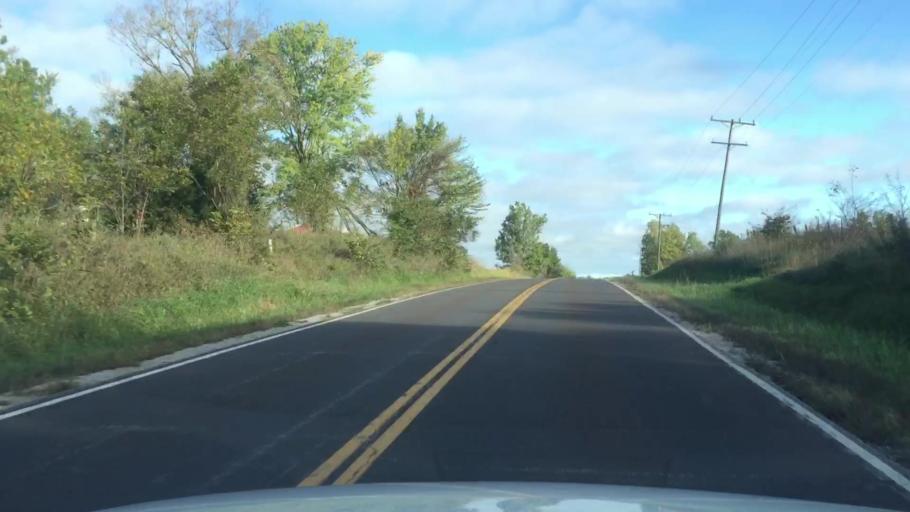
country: US
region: Missouri
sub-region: Howard County
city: New Franklin
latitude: 39.0519
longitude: -92.7444
